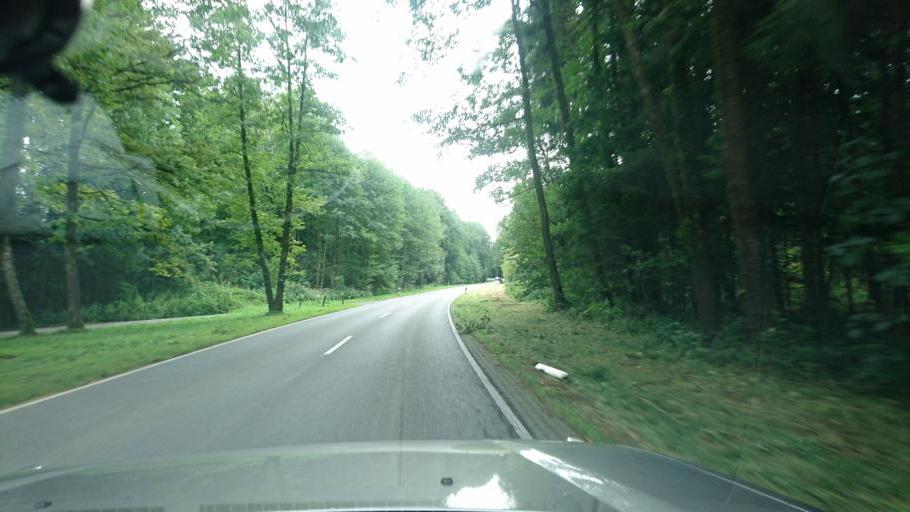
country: DE
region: Bavaria
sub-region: Upper Bavaria
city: Chieming
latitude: 47.9184
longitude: 12.5128
